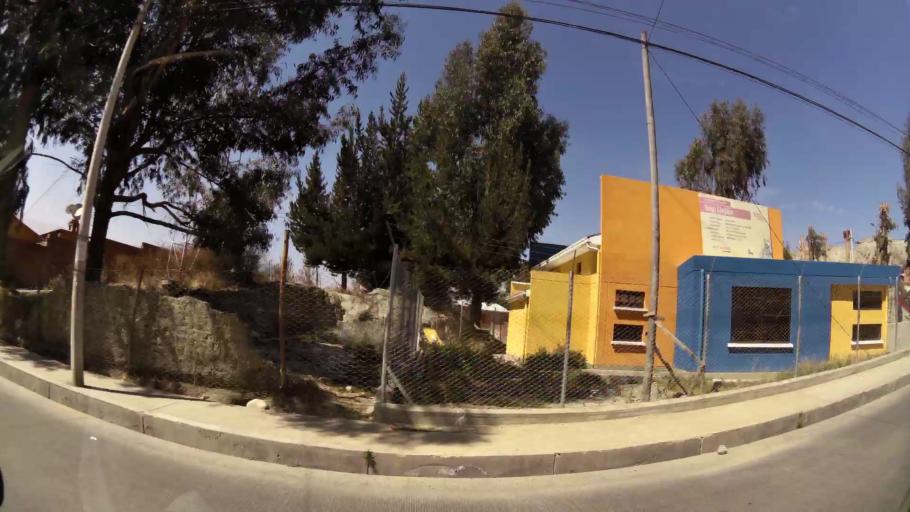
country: BO
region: La Paz
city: La Paz
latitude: -16.5304
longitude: -68.1258
